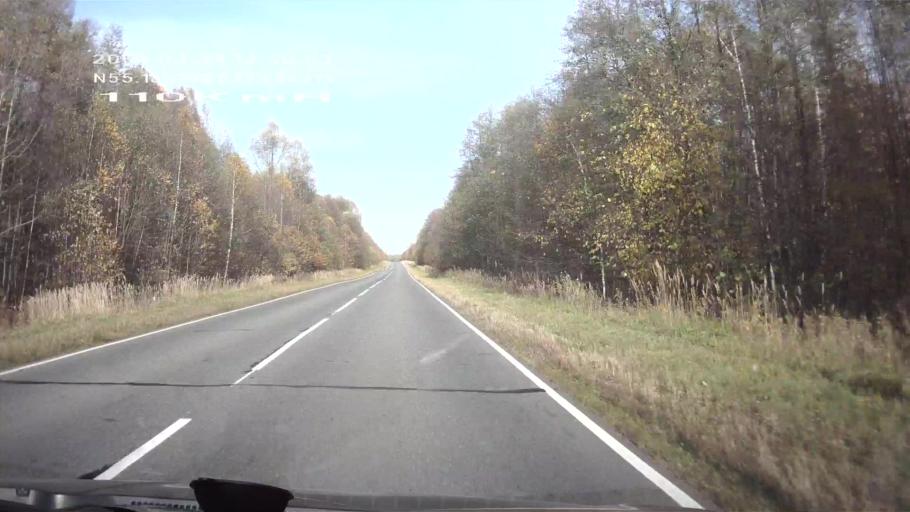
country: RU
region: Chuvashia
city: Buinsk
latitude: 55.1805
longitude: 47.0642
